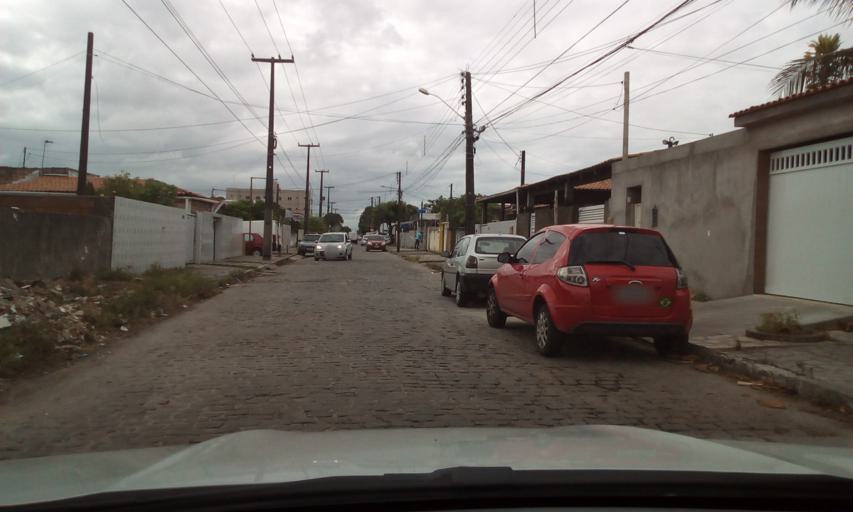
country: BR
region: Paraiba
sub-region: Joao Pessoa
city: Joao Pessoa
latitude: -7.1563
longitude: -34.8743
